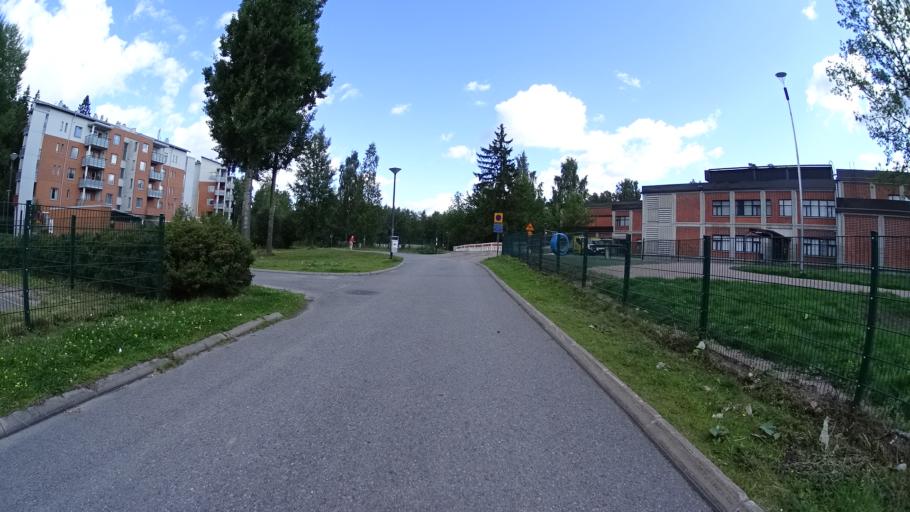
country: FI
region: Uusimaa
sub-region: Helsinki
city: Kilo
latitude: 60.2571
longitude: 24.8051
